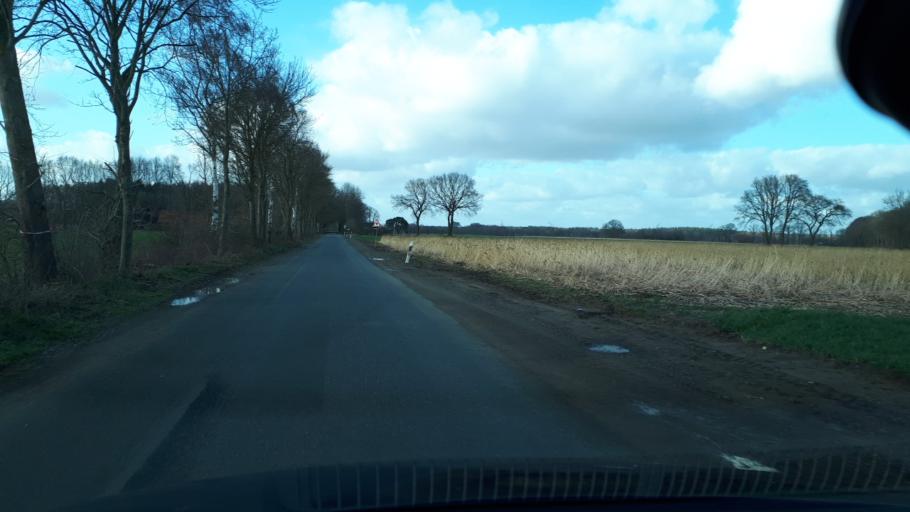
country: DE
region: Lower Saxony
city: Cloppenburg
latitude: 52.8411
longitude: 7.9971
